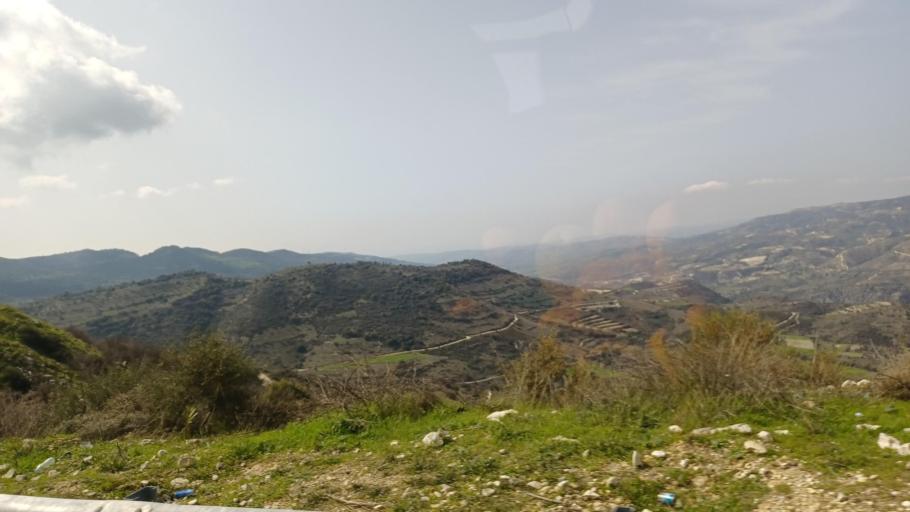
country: CY
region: Limassol
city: Pachna
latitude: 34.7947
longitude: 32.7383
